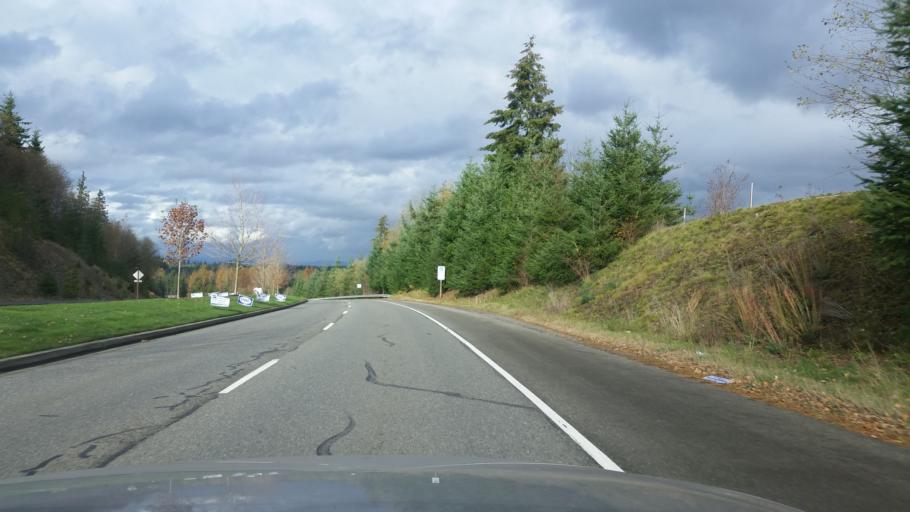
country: US
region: Washington
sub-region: King County
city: Fall City
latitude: 47.5176
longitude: -121.8789
